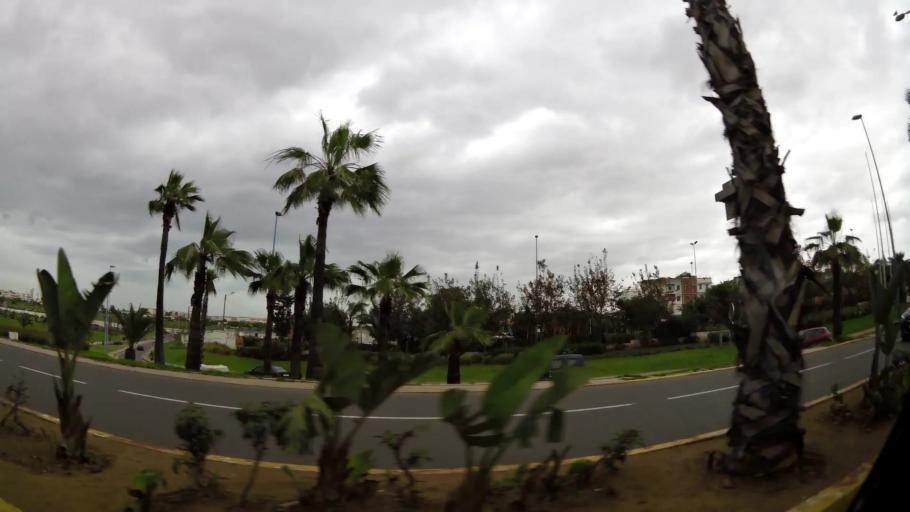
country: MA
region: Grand Casablanca
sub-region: Casablanca
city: Casablanca
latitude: 33.5665
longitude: -7.5726
